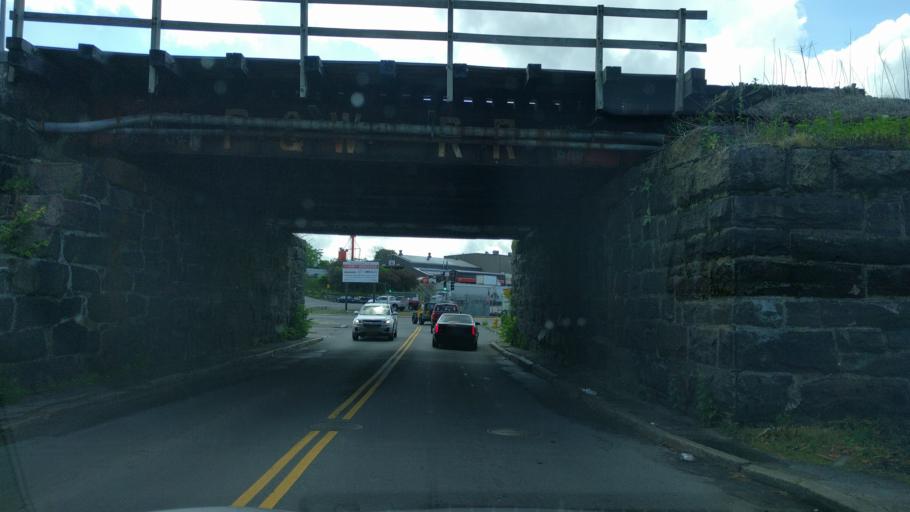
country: US
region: Massachusetts
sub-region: Worcester County
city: Worcester
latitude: 42.2512
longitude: -71.8097
